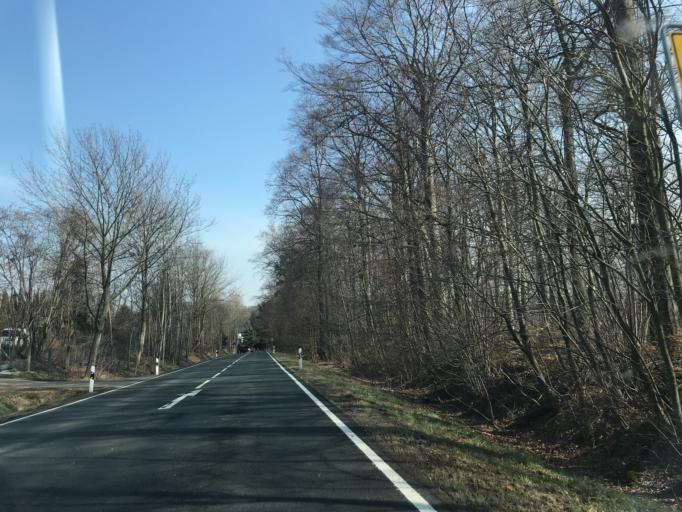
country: DE
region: Saxony
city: Rochlitz
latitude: 51.0407
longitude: 12.7838
